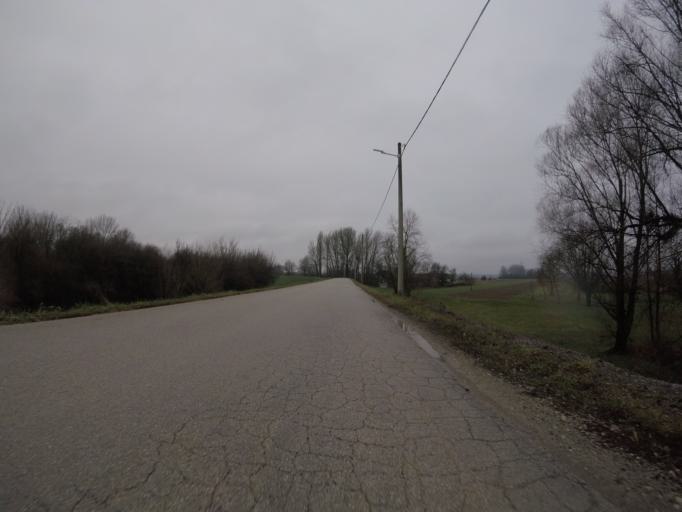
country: HR
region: Sisacko-Moslavacka
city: Lekenik
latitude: 45.6709
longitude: 16.2447
